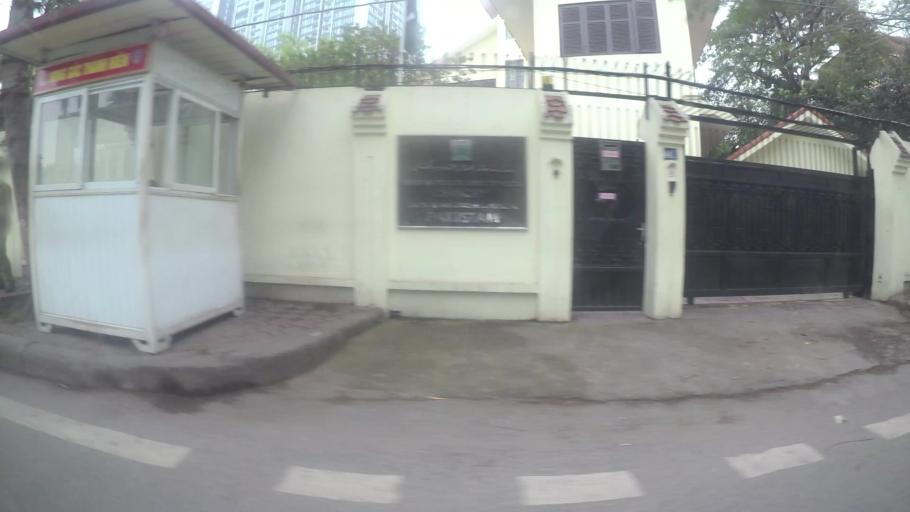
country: VN
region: Ha Noi
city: Cau Giay
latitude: 21.0325
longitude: 105.8171
